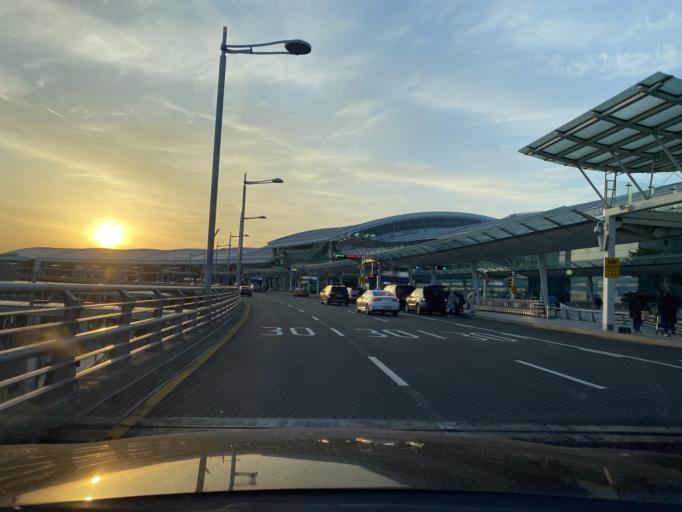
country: KR
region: Incheon
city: Incheon
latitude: 37.4492
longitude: 126.4533
